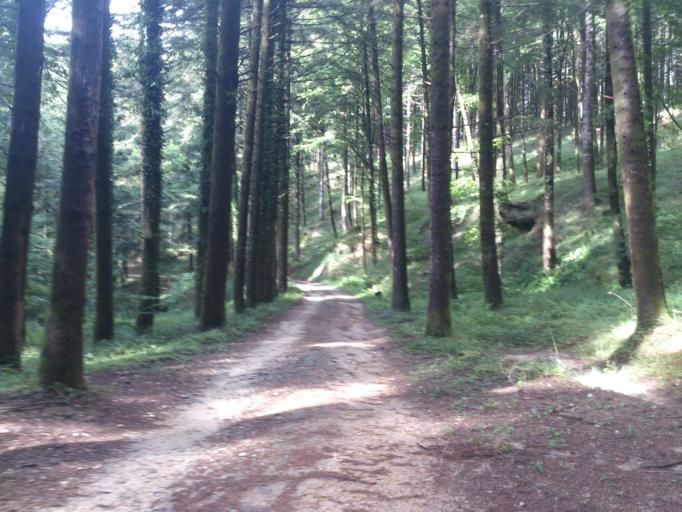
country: IT
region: Calabria
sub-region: Provincia di Vibo-Valentia
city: Serra San Bruno
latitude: 38.5501
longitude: 16.3108
